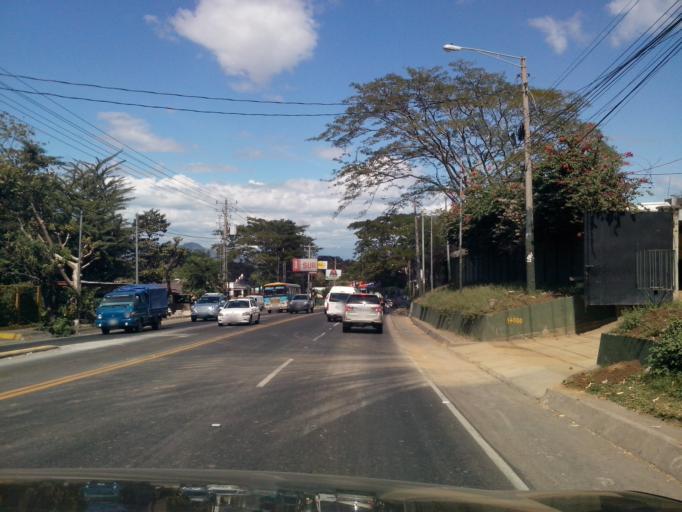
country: NI
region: Managua
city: Ciudad Sandino
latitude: 12.1168
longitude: -86.3152
